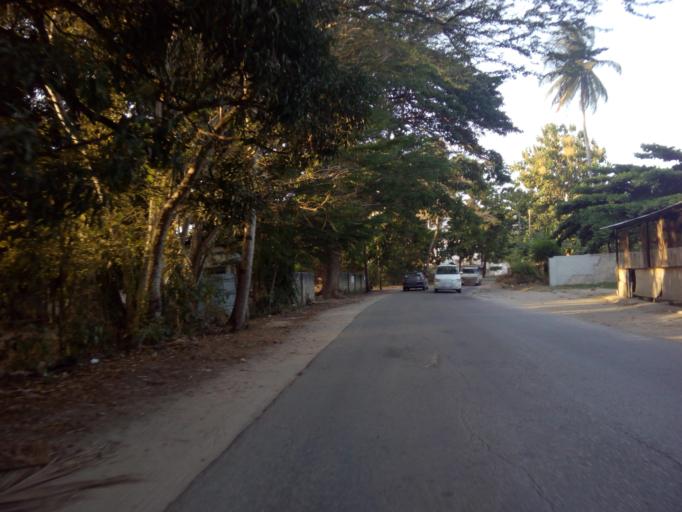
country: TZ
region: Zanzibar Urban/West
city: Zanzibar
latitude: -6.2014
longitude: 39.2107
